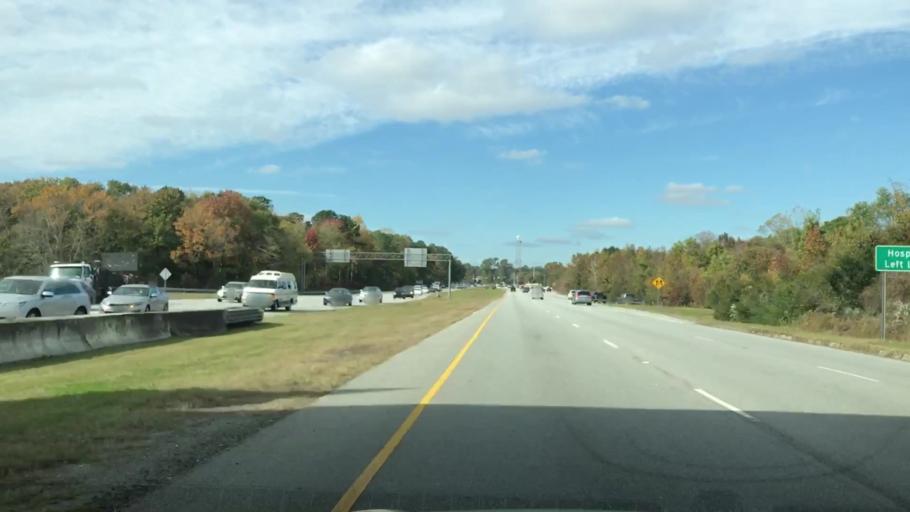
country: US
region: South Carolina
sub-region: Charleston County
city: Shell Point
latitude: 32.8098
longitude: -80.0369
